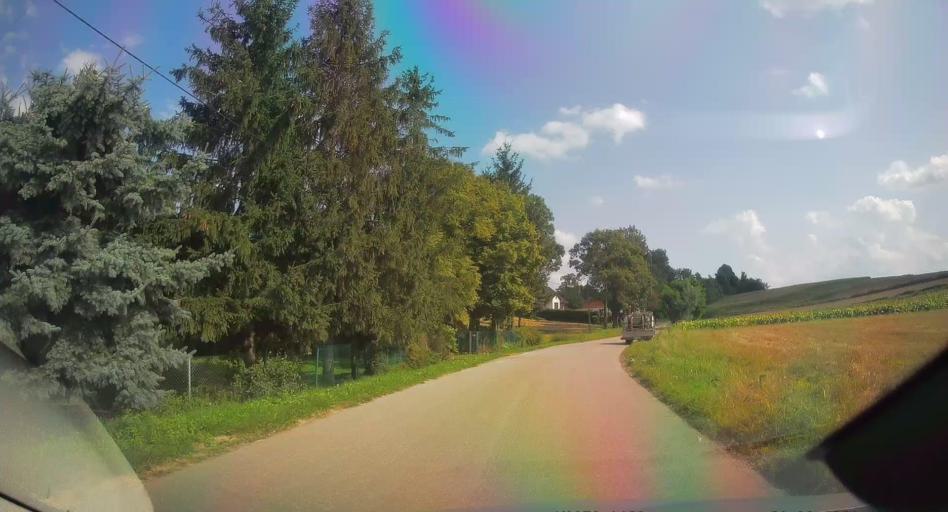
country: PL
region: Lesser Poland Voivodeship
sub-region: Powiat bochenski
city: Dziewin
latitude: 50.1569
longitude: 20.4607
